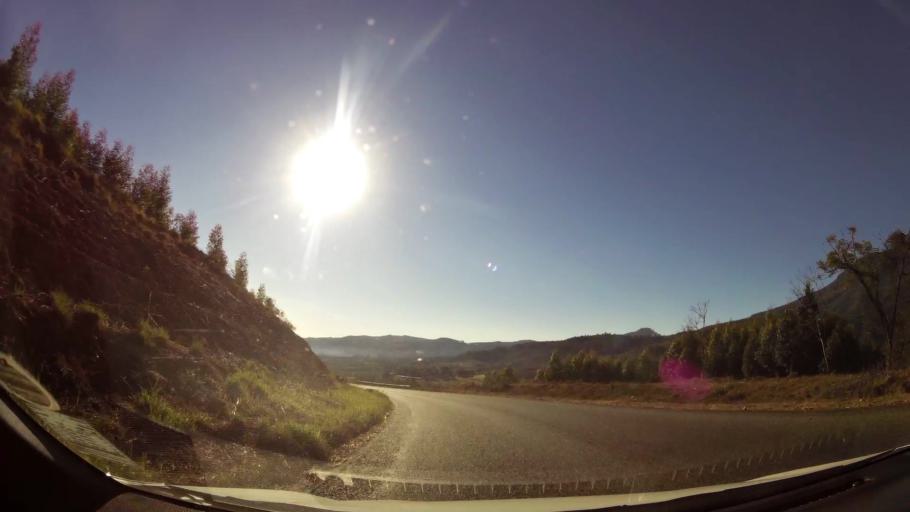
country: ZA
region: Limpopo
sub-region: Mopani District Municipality
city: Tzaneen
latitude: -23.9466
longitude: 30.0157
